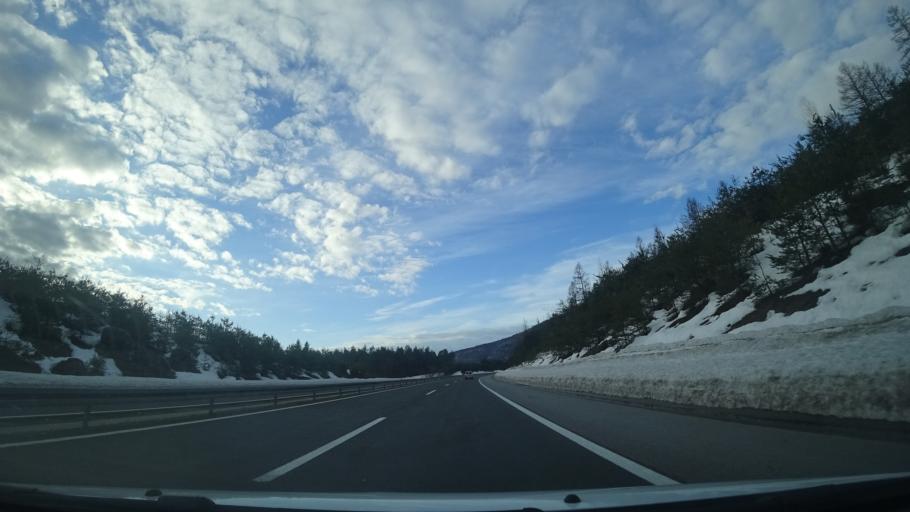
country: HR
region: Karlovacka
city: Ostarije
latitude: 45.2034
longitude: 15.2651
